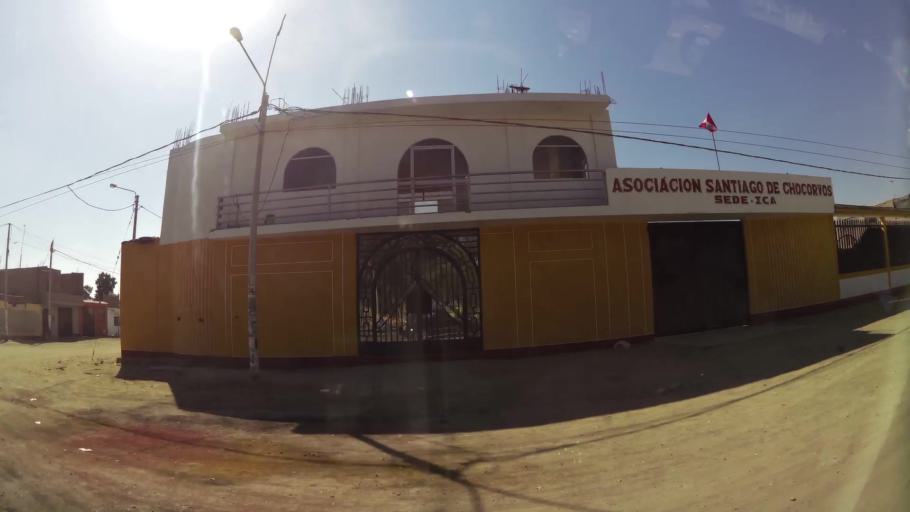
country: PE
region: Ica
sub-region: Provincia de Ica
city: La Tinguina
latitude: -14.0387
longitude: -75.7039
